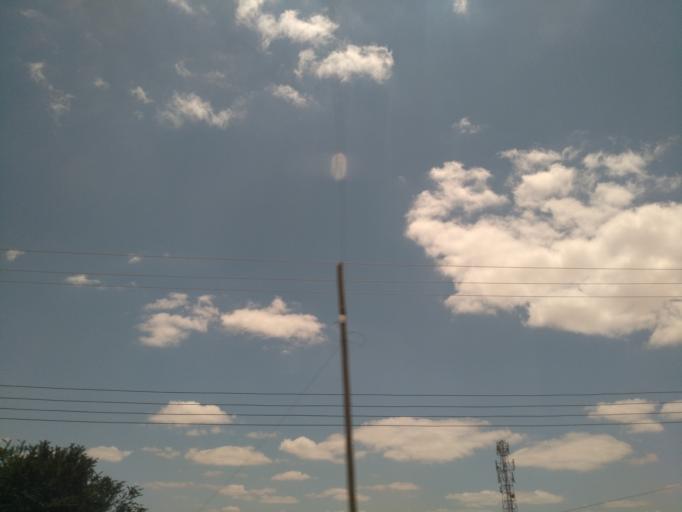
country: TZ
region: Dodoma
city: Kisasa
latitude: -6.1642
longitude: 35.7714
